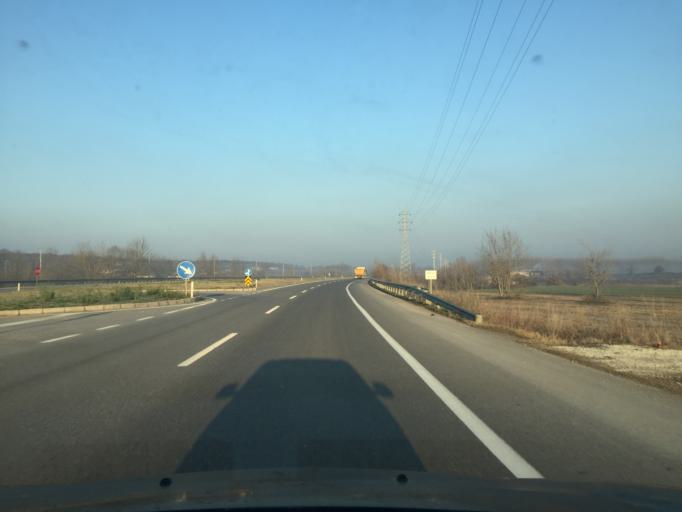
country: TR
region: Sakarya
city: Akyazi
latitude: 40.6488
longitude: 30.6058
